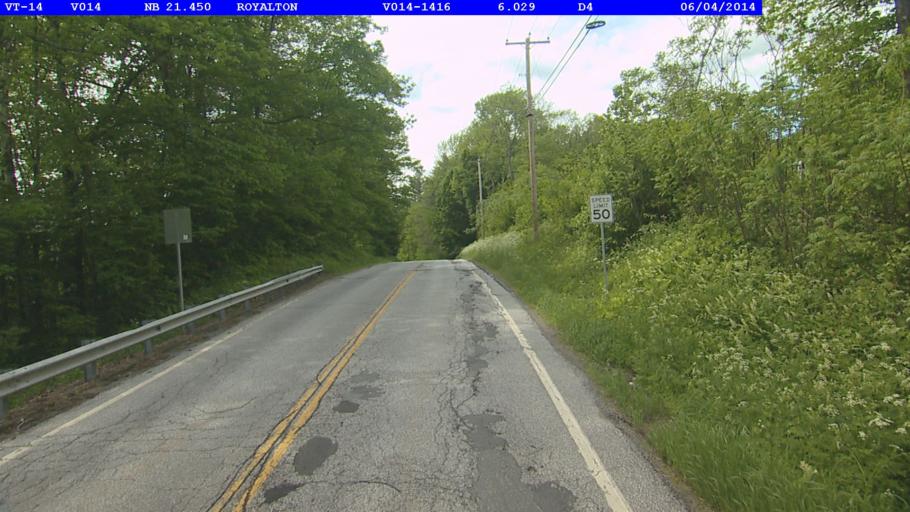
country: US
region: Vermont
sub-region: Orange County
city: Randolph
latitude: 43.8290
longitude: -72.5677
